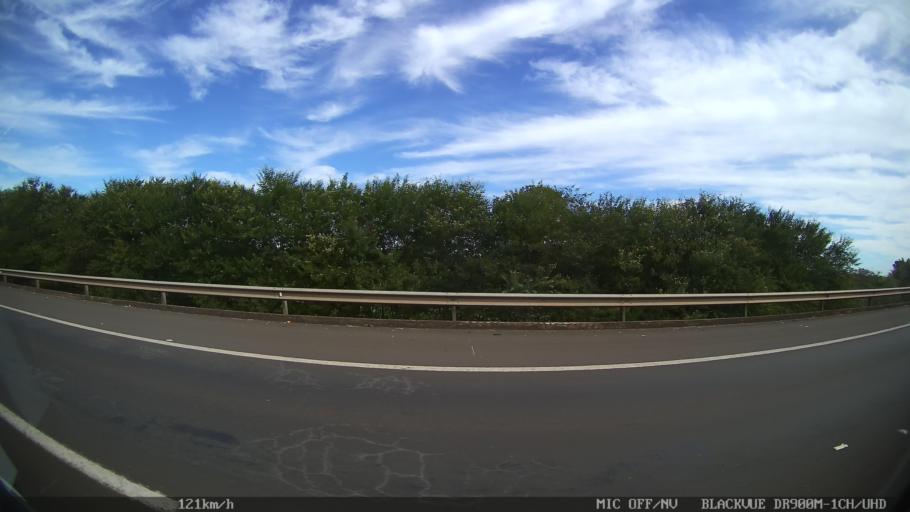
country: BR
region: Sao Paulo
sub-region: Matao
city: Matao
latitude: -21.5723
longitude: -48.4605
